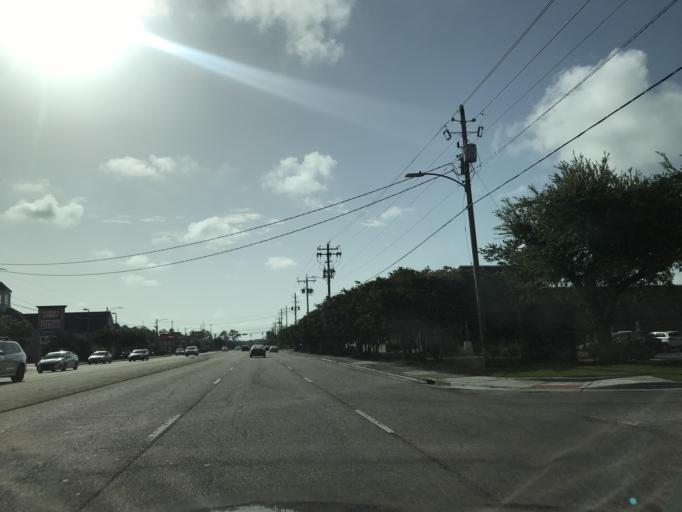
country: US
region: North Carolina
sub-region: New Hanover County
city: Wilmington
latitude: 34.2156
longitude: -77.9035
